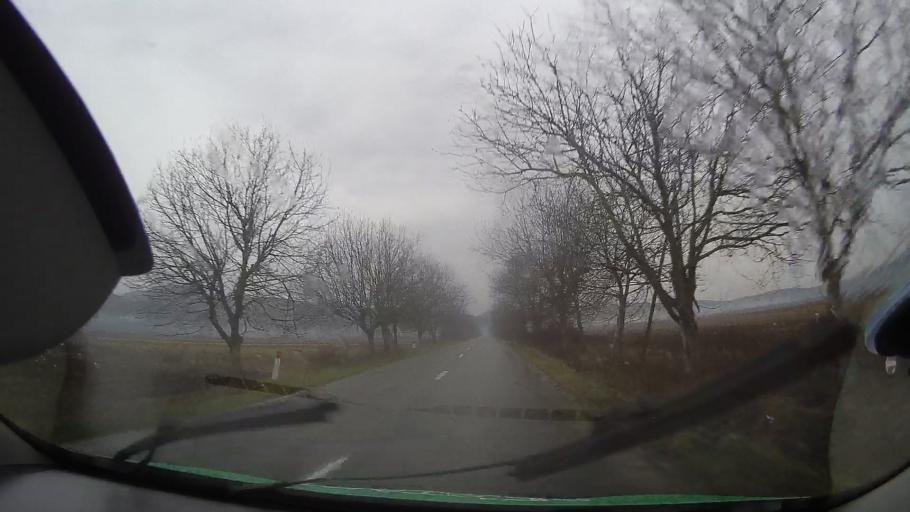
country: RO
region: Bihor
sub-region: Comuna Uileacu de Beius
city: Uileacu de Beius
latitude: 46.6808
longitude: 22.2405
